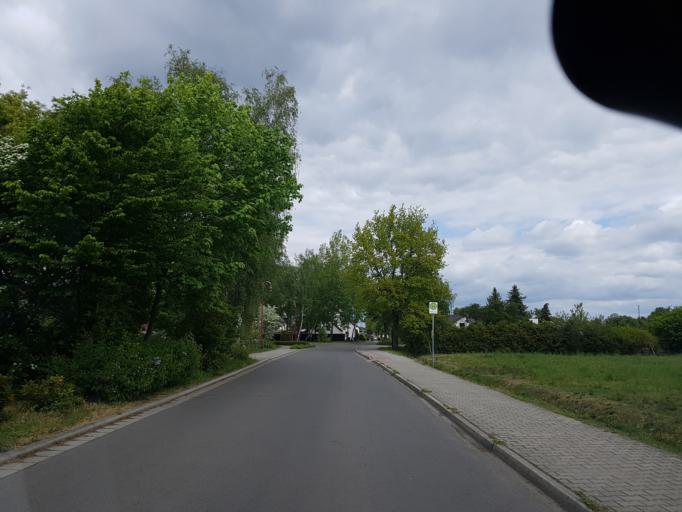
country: DE
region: Brandenburg
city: Altdobern
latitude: 51.6502
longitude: 14.0199
